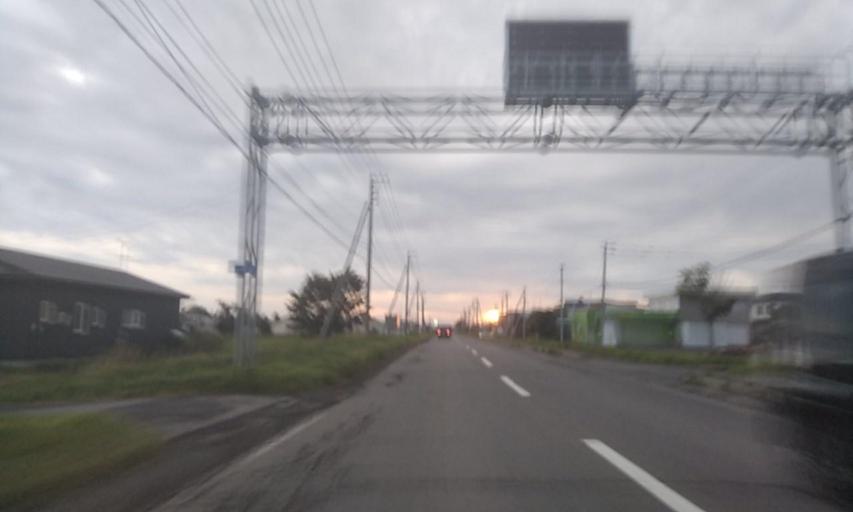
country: JP
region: Hokkaido
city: Abashiri
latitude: 43.9014
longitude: 144.6761
